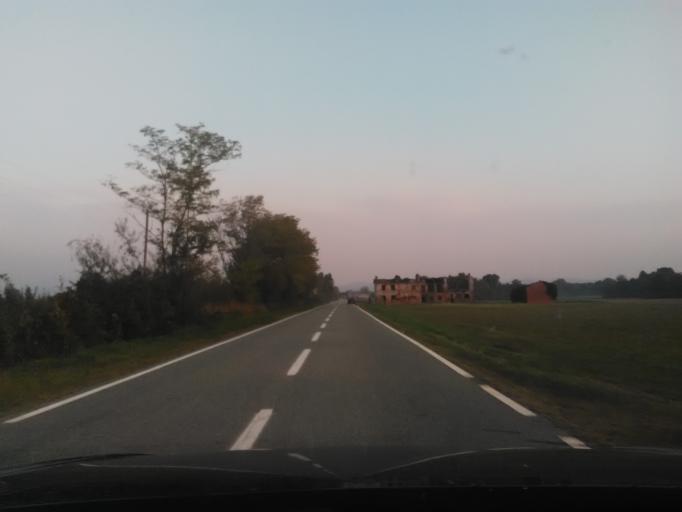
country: IT
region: Piedmont
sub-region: Provincia di Vercelli
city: Rovasenda
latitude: 45.5445
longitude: 8.3022
